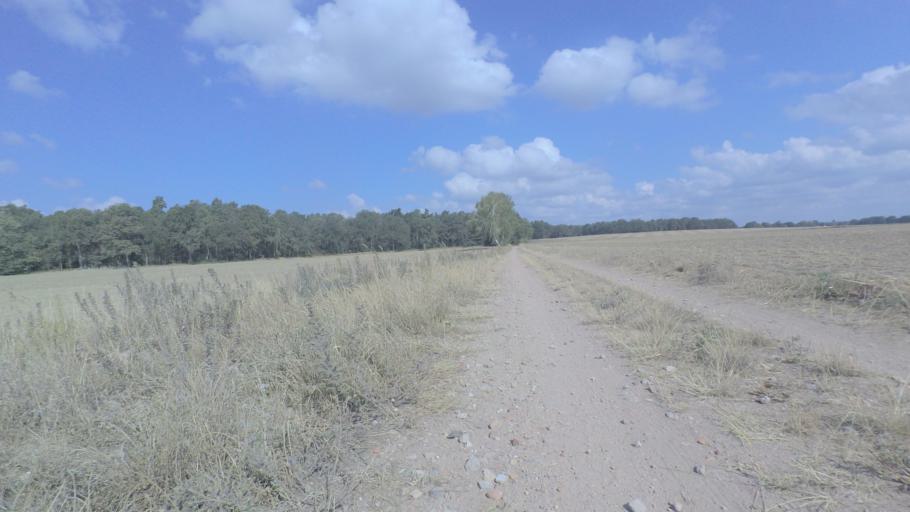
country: DE
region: Brandenburg
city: Walsleben
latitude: 52.9503
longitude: 12.6977
